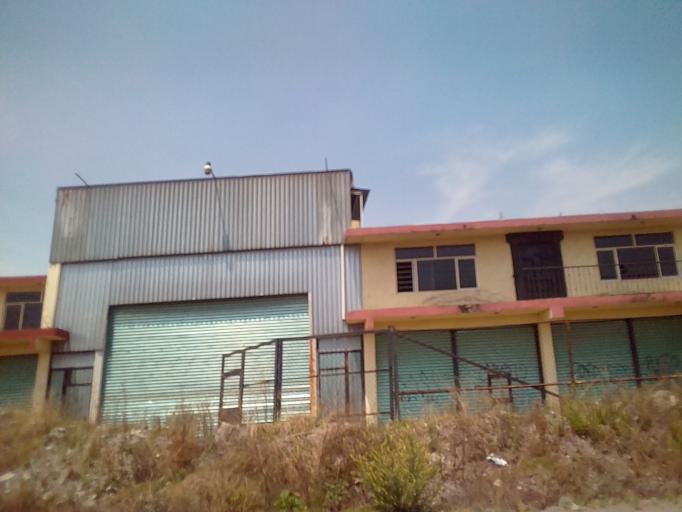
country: MX
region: Mexico
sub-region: Toluca
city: Guadalupe Totoltepec
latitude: 19.3487
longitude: -99.5578
